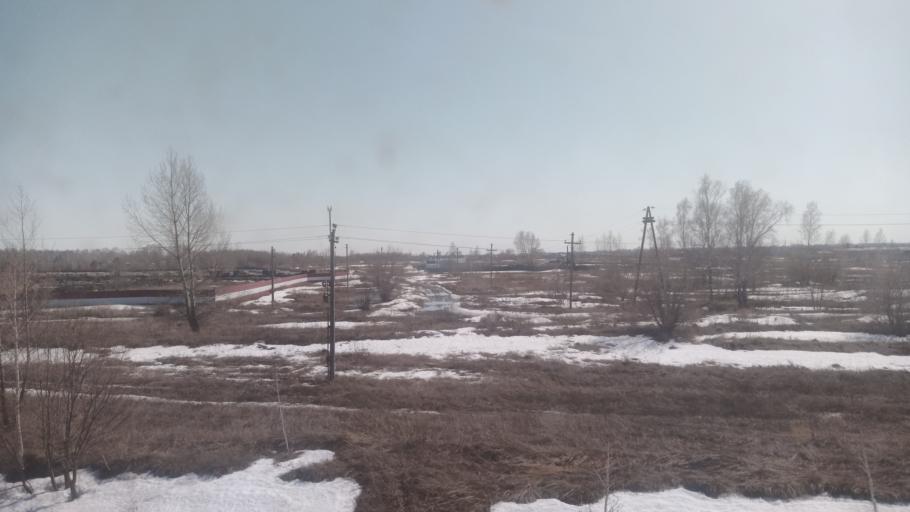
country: RU
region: Altai Krai
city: Beloyarsk
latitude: 53.4485
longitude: 83.9710
